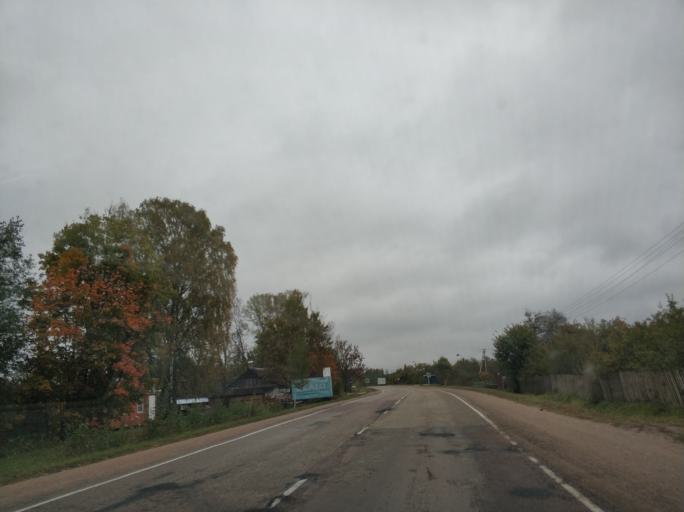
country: BY
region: Vitebsk
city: Rasony
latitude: 56.0553
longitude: 28.7125
